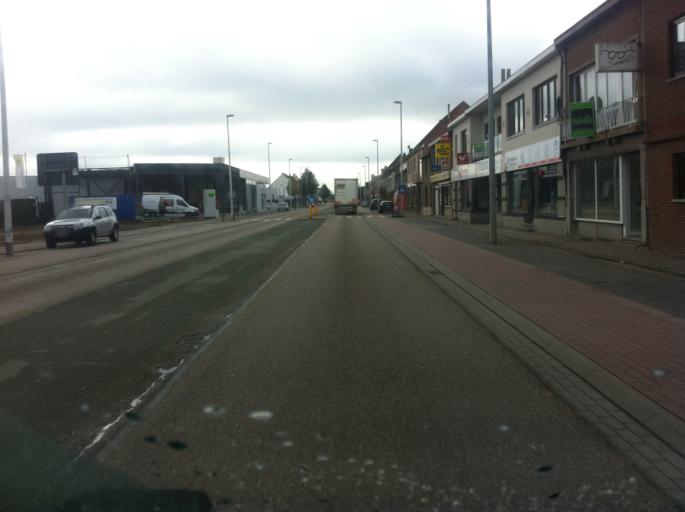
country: BE
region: Flanders
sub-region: Provincie Limburg
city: Maasmechelen
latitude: 50.9220
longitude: 5.6856
